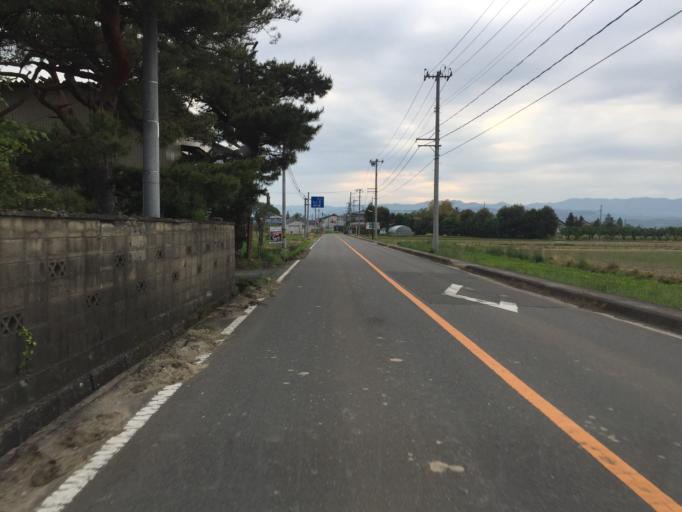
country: JP
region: Fukushima
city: Hobaramachi
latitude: 37.8500
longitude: 140.5481
